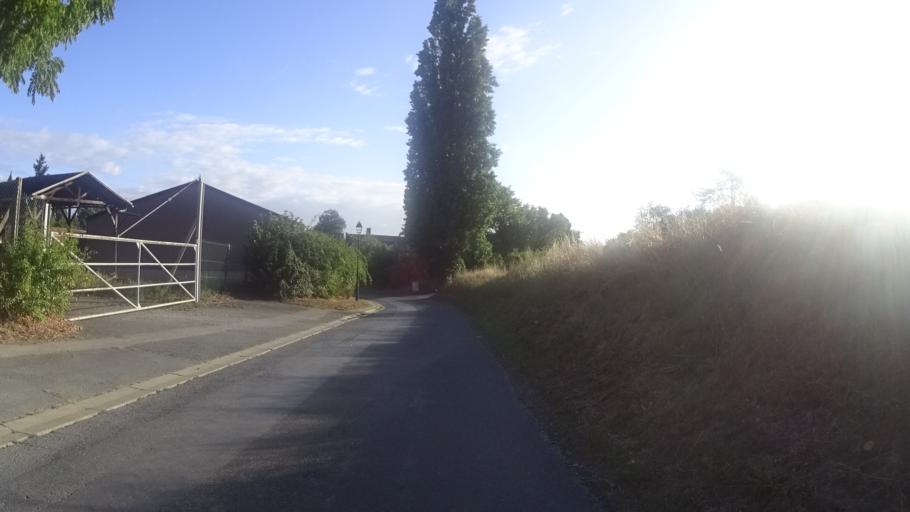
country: FR
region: Picardie
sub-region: Departement de l'Oise
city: Verberie
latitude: 49.3059
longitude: 2.6958
